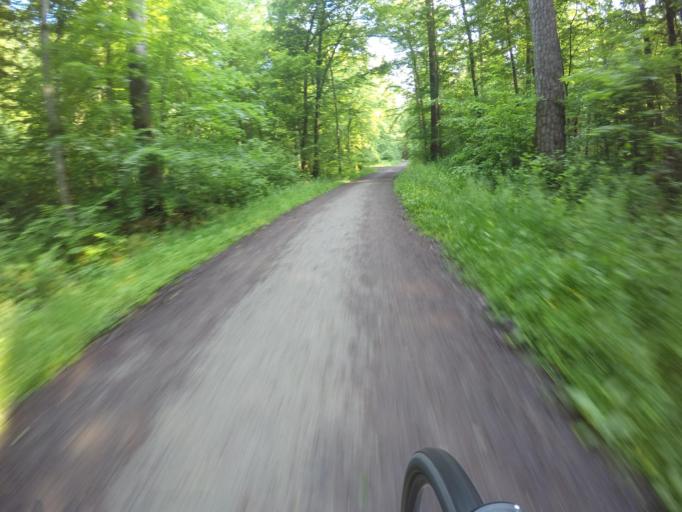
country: DE
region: Baden-Wuerttemberg
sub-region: Regierungsbezirk Stuttgart
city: Gerlingen
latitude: 48.7438
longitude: 9.0735
